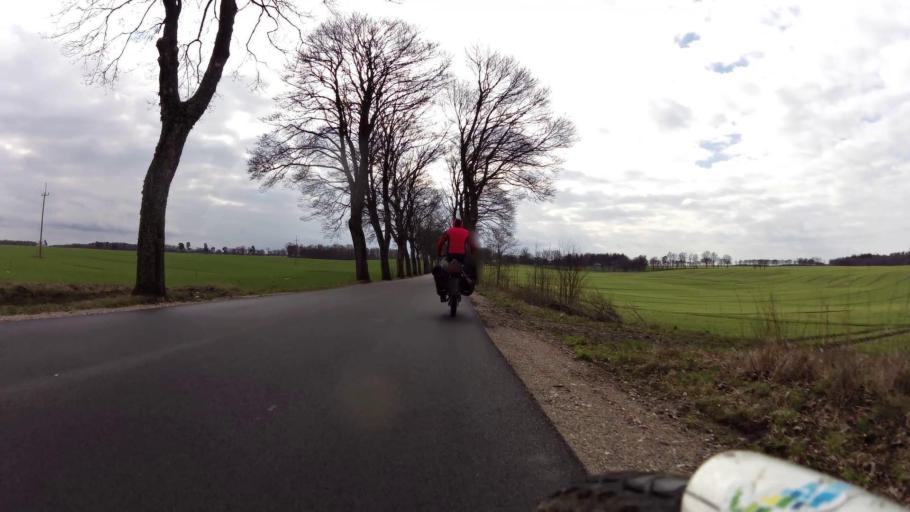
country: PL
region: Pomeranian Voivodeship
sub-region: Powiat bytowski
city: Kolczyglowy
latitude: 54.2293
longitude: 17.2419
